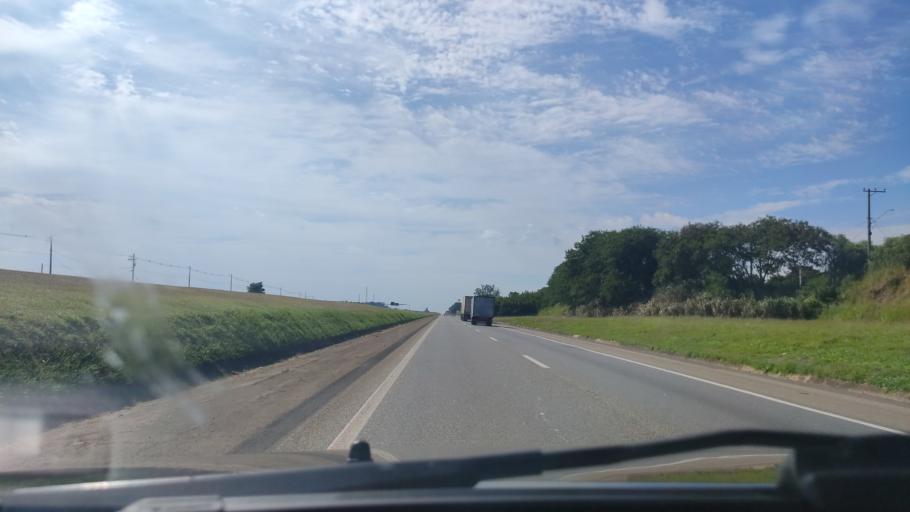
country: BR
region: Sao Paulo
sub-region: Boituva
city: Boituva
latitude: -23.3182
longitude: -47.6268
